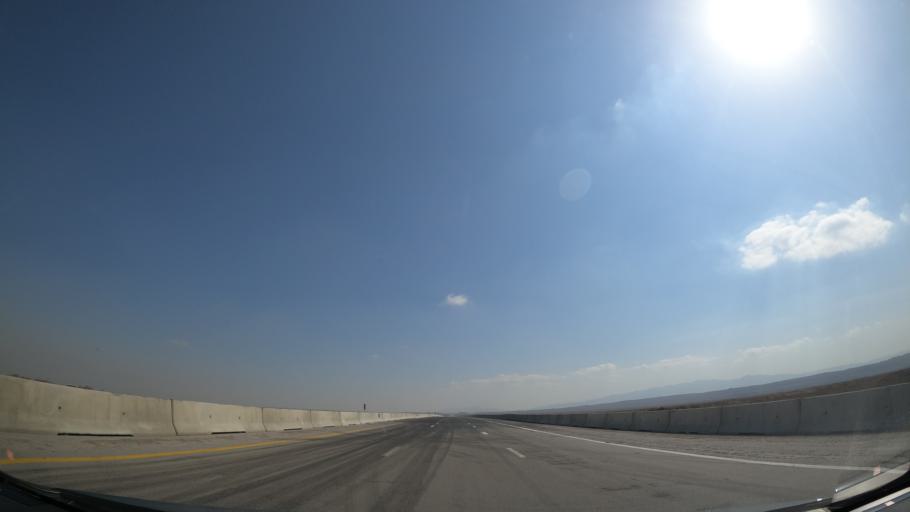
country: IR
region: Alborz
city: Nazarabad
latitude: 35.8375
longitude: 50.4912
